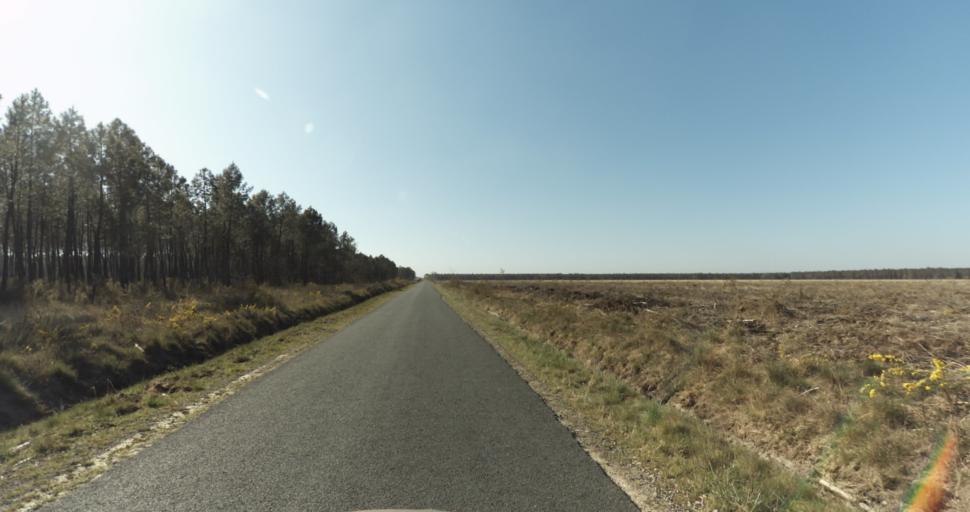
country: FR
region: Aquitaine
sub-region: Departement de la Gironde
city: Marcheprime
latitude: 44.7834
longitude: -0.8616
